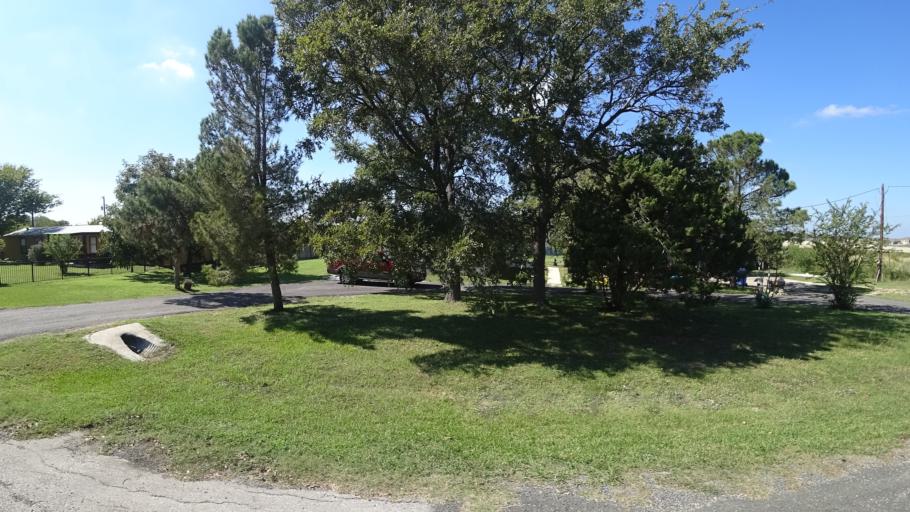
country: US
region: Texas
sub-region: Travis County
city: Manor
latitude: 30.3489
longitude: -97.6042
